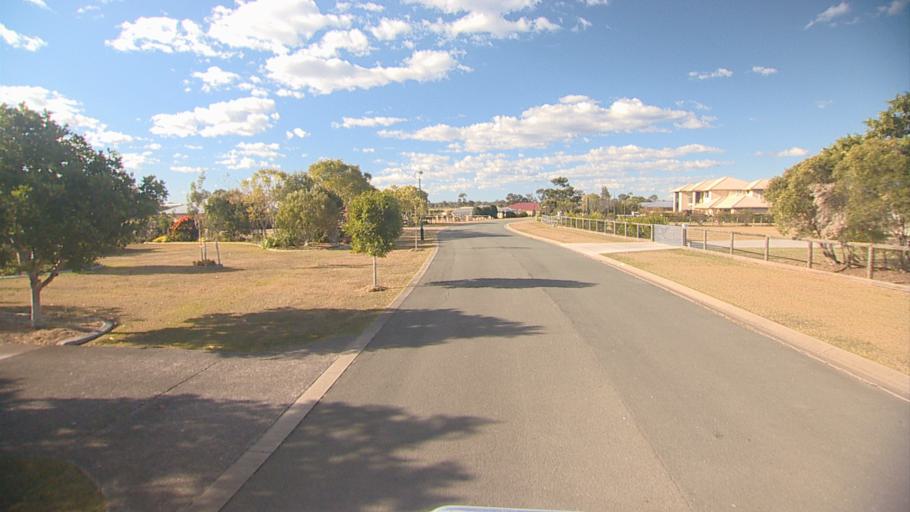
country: AU
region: Queensland
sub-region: Logan
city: North Maclean
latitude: -27.8261
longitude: 153.0025
